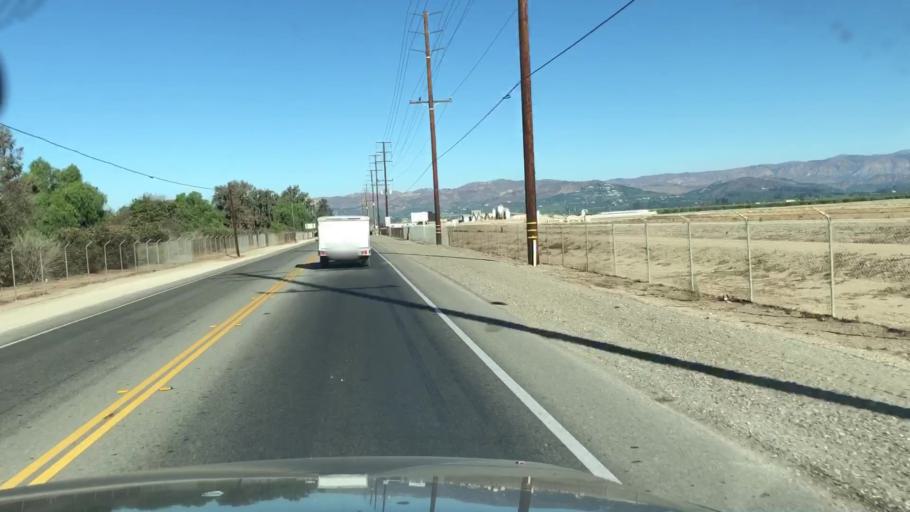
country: US
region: California
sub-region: Ventura County
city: Saticoy
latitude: 34.2701
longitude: -119.1296
